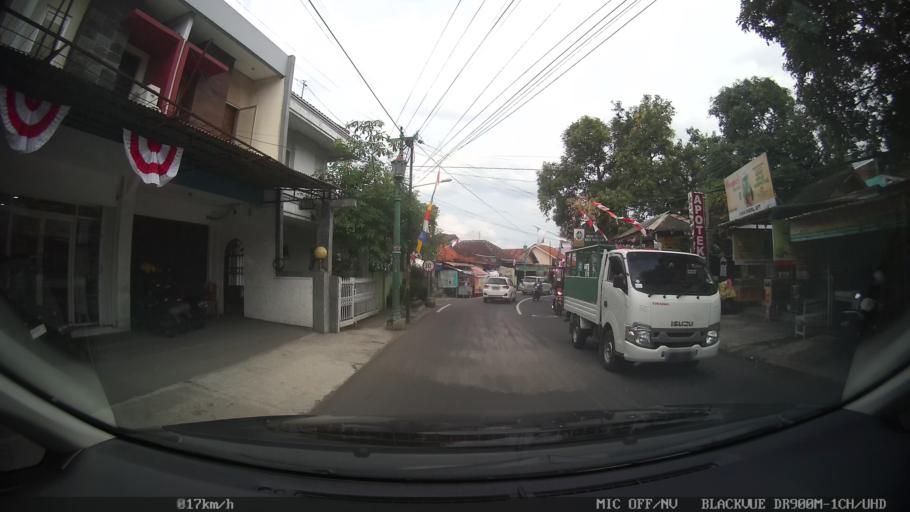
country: ID
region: Daerah Istimewa Yogyakarta
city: Yogyakarta
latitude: -7.7868
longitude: 110.3952
